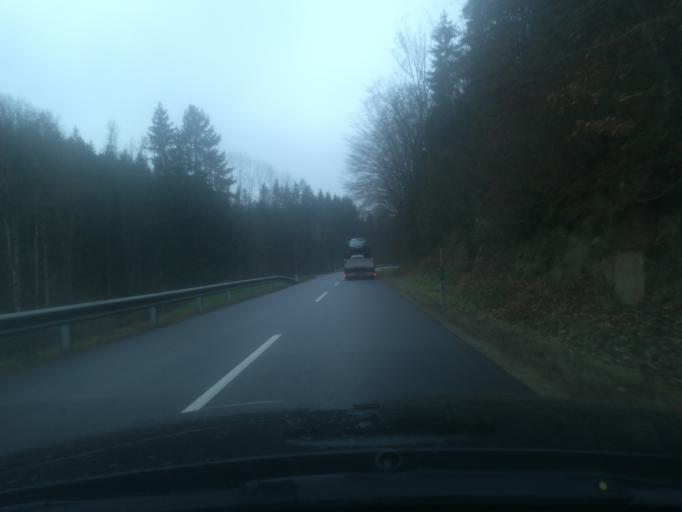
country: AT
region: Upper Austria
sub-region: Politischer Bezirk Perg
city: Perg
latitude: 48.3183
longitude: 14.5799
